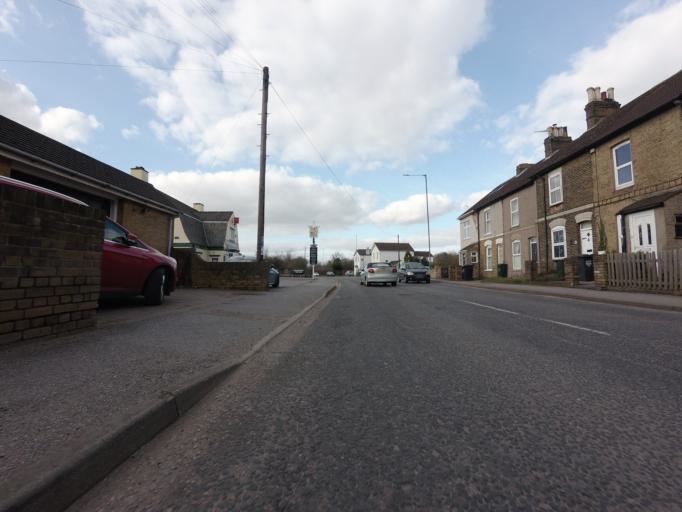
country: GB
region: England
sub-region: Kent
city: Dartford
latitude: 51.4211
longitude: 0.2315
